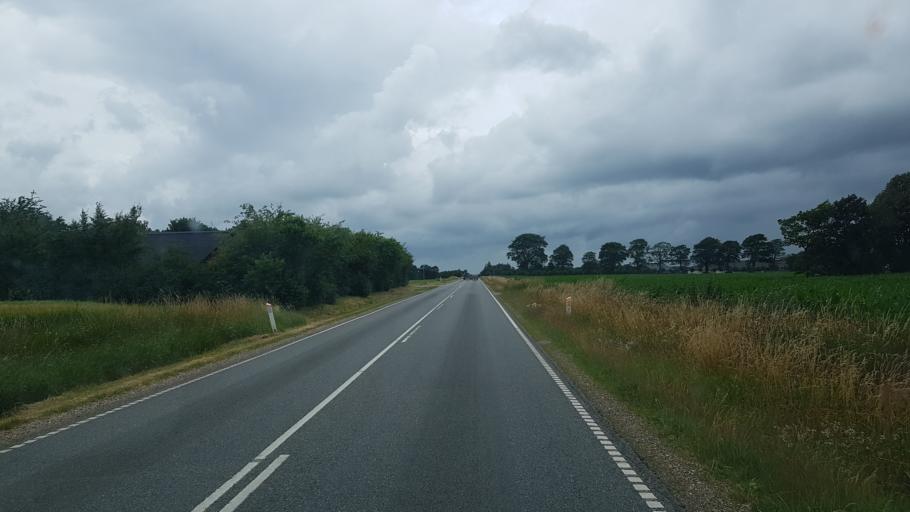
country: DK
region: South Denmark
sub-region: Kolding Kommune
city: Vamdrup
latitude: 55.4330
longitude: 9.2182
